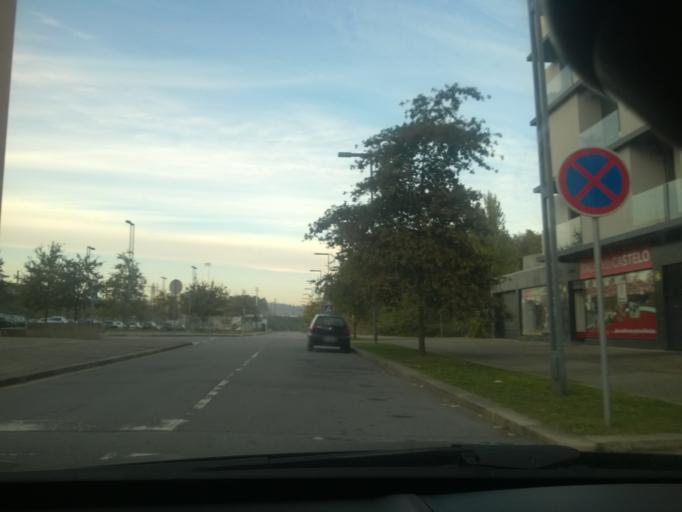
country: PT
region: Porto
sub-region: Maia
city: Anta
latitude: 41.2679
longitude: -8.6144
